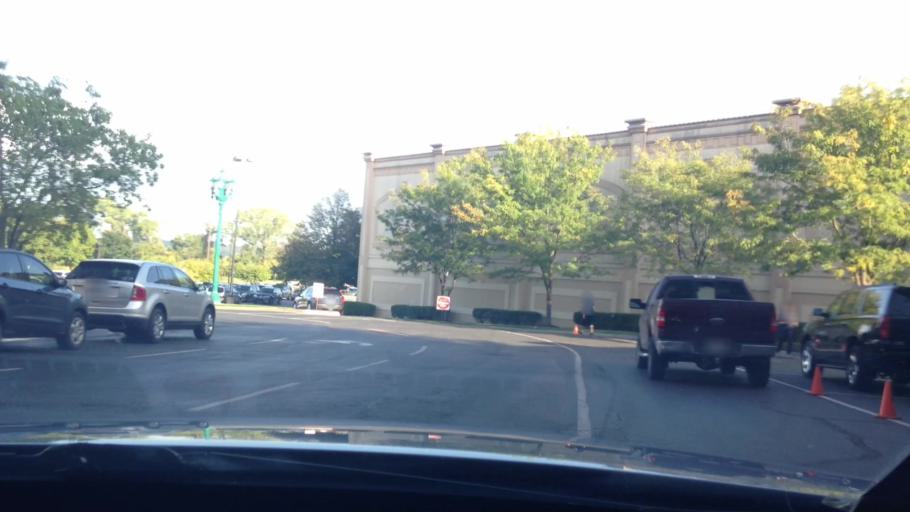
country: US
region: Missouri
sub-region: Clay County
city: Claycomo
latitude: 39.1500
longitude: -94.4831
